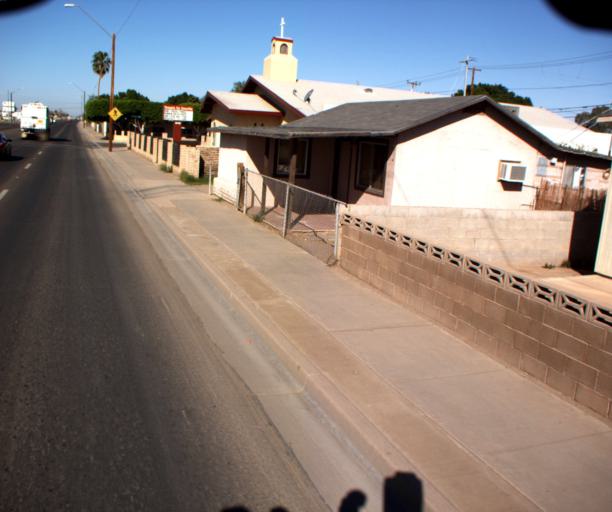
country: US
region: Arizona
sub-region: Yuma County
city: Somerton
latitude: 32.5967
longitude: -114.7155
